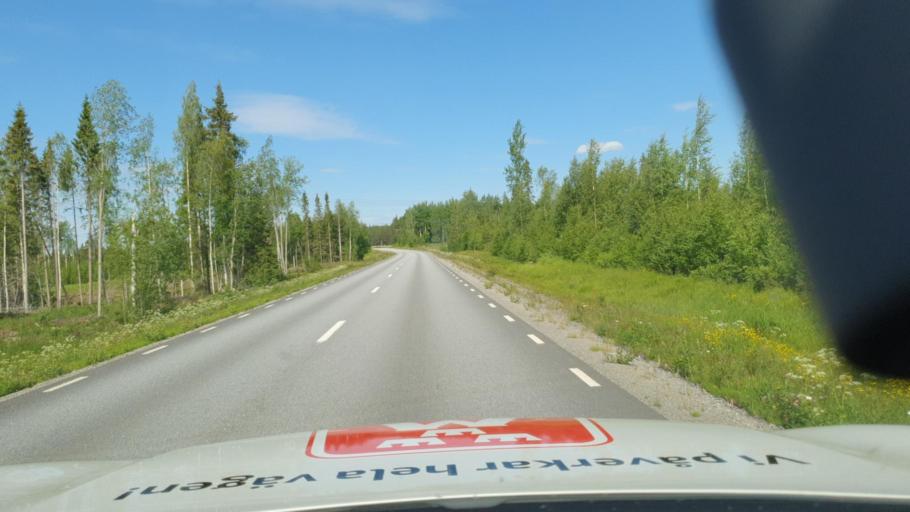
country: SE
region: Vaesterbotten
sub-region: Skelleftea Kommun
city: Forsbacka
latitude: 64.7216
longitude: 20.4154
